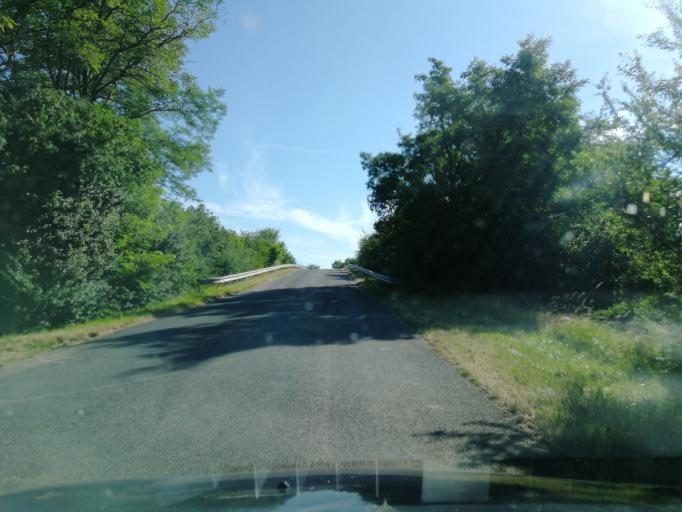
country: FR
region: Rhone-Alpes
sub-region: Departement du Rhone
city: Sathonay-Village
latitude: 45.8405
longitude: 4.8889
